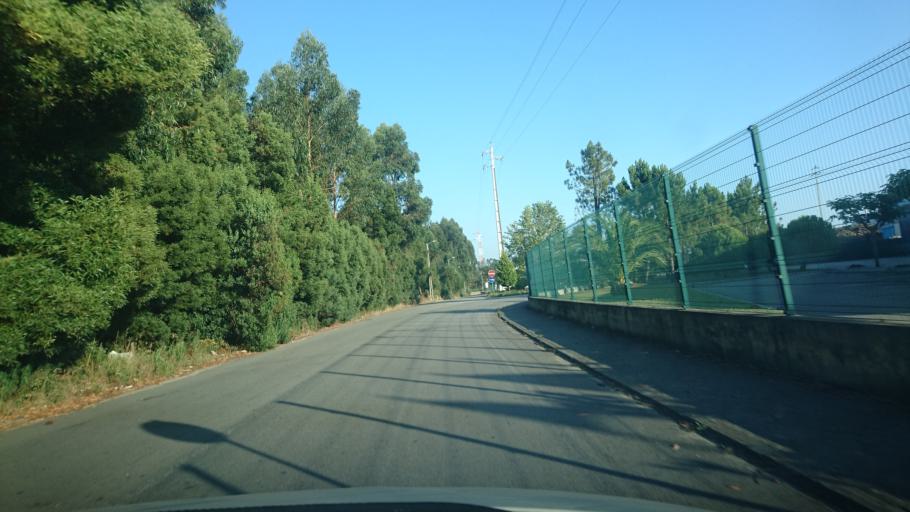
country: PT
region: Aveiro
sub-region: Ovar
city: Esmoriz
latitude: 40.9641
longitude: -8.6107
